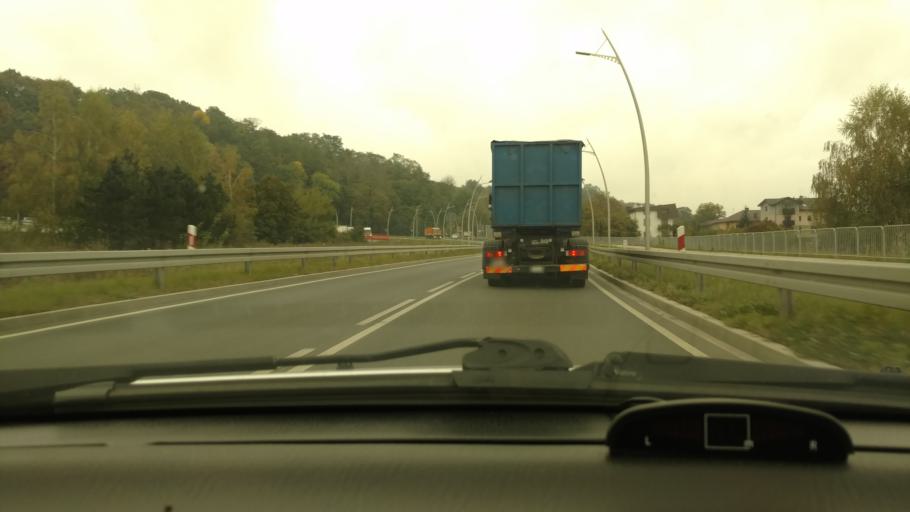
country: PL
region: Lesser Poland Voivodeship
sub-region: Powiat nowosadecki
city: Nowy Sacz
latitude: 49.6404
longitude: 20.6902
